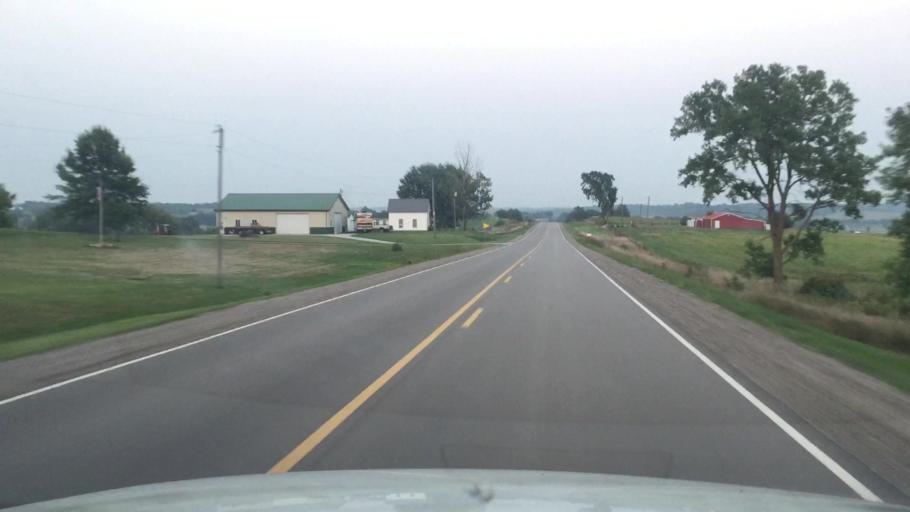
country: US
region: Iowa
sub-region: Marion County
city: Melcher-Dallas
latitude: 41.1893
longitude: -93.4038
